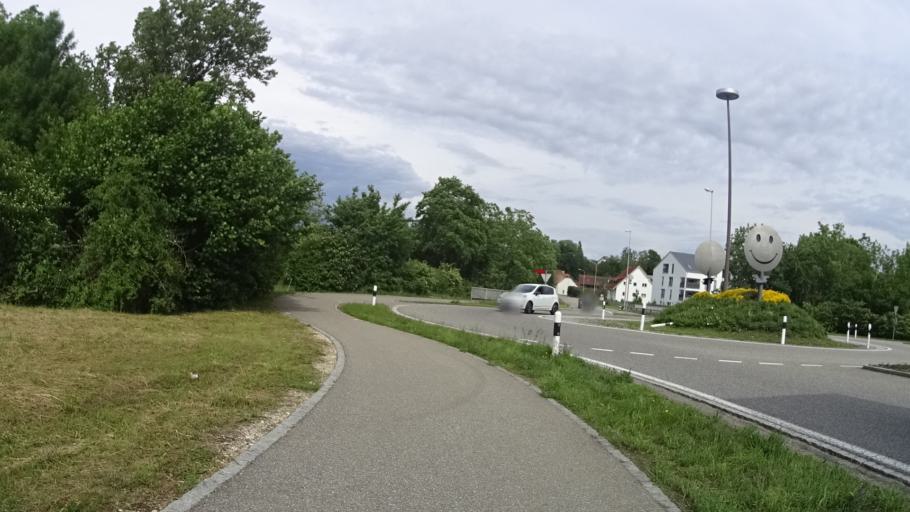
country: CH
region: Aargau
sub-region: Bezirk Laufenburg
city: Eiken
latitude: 47.5519
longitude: 7.9836
